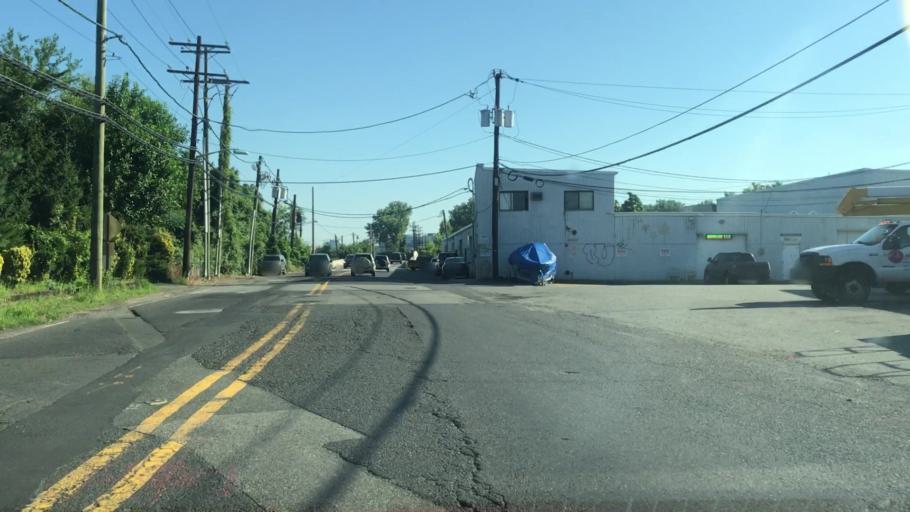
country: US
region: New Jersey
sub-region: Bergen County
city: Ridgefield
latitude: 40.8376
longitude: -74.0175
